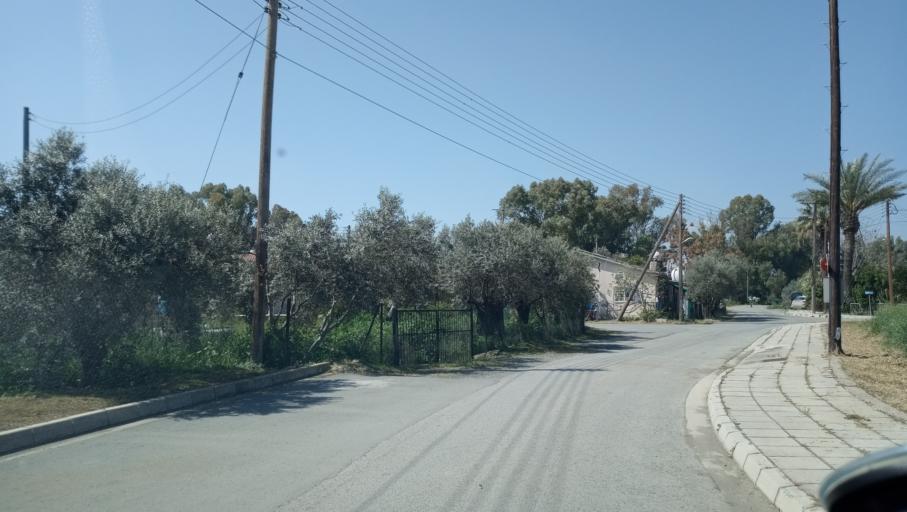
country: CY
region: Lefkosia
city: Alampra
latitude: 35.0192
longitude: 33.3872
